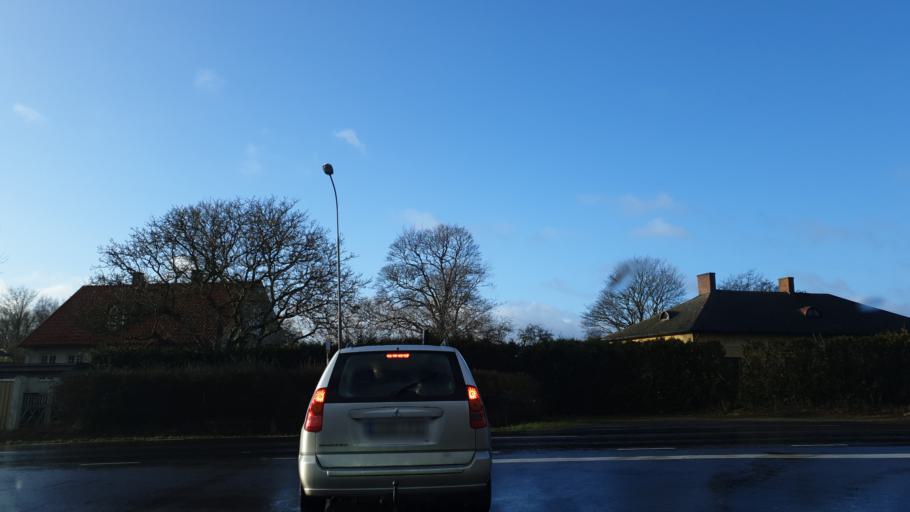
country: SE
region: Skane
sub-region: Skurups Kommun
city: Rydsgard
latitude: 55.4512
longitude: 13.5467
